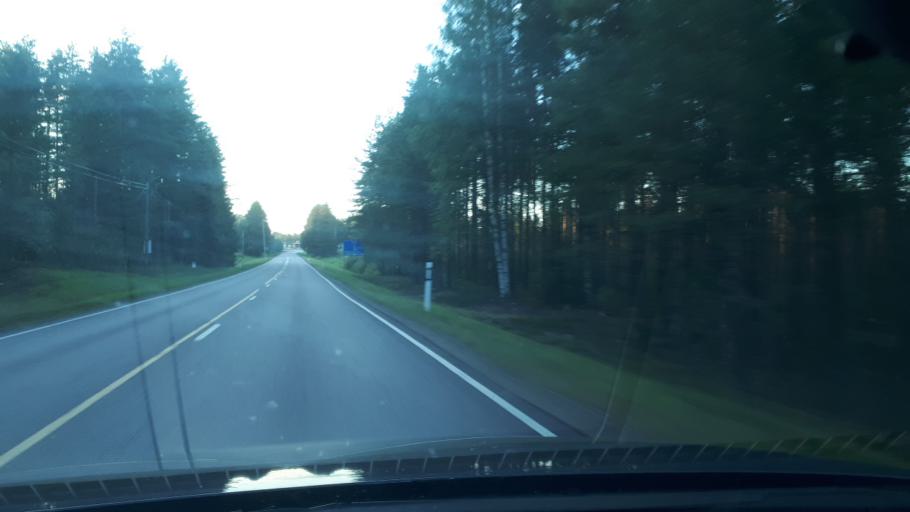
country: FI
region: Northern Ostrobothnia
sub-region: Haapavesi-Siikalatva
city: Pulkkila
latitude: 64.2600
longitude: 25.8743
